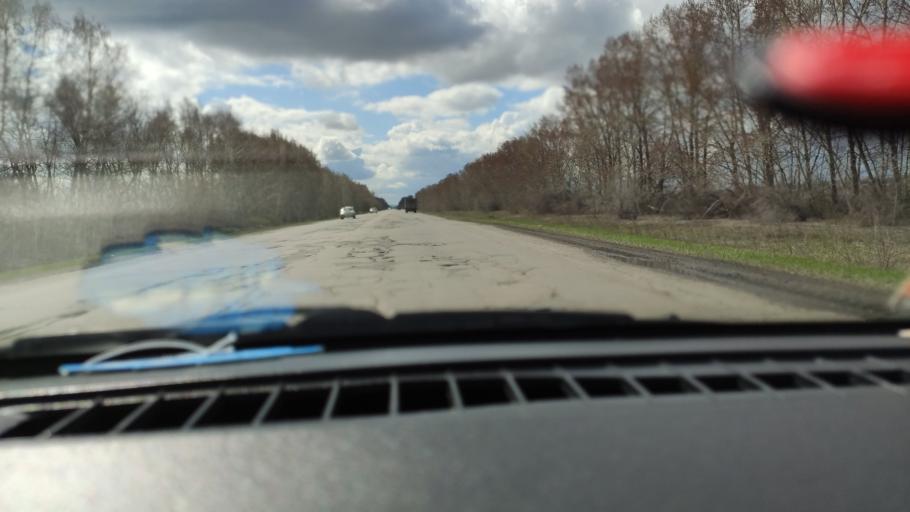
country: RU
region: Samara
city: Tol'yatti
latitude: 53.6369
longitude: 49.4191
